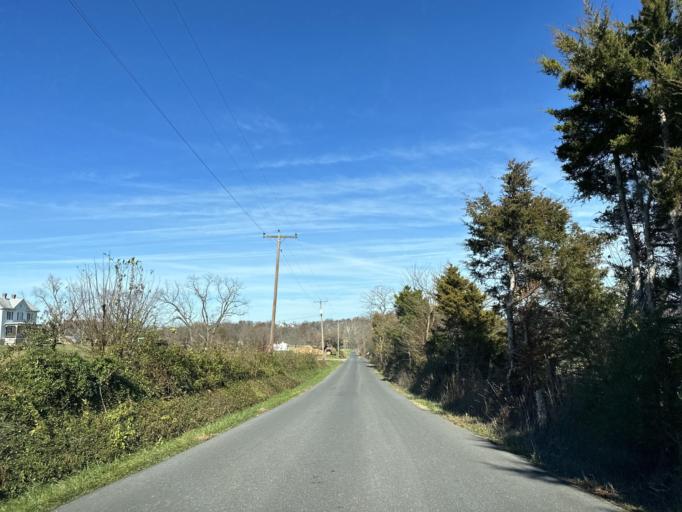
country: US
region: Virginia
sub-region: Augusta County
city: Weyers Cave
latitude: 38.2255
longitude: -78.9245
